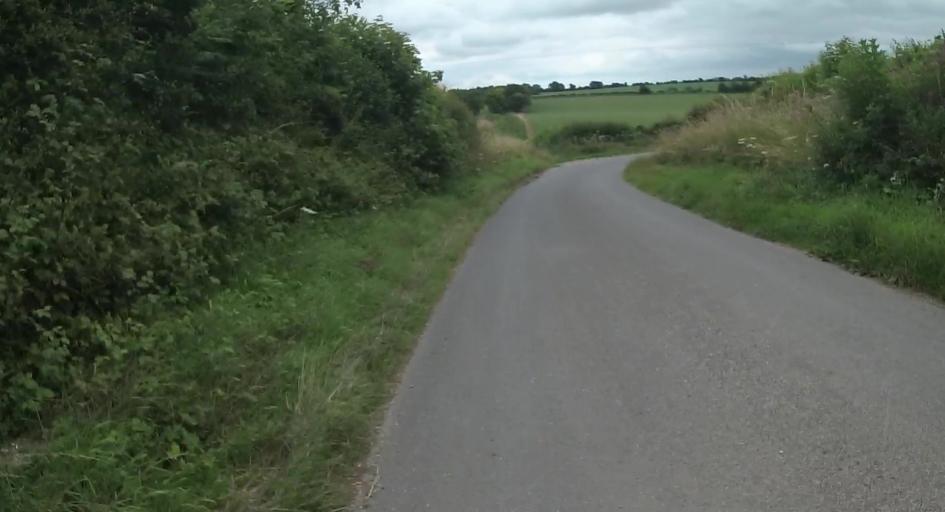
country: GB
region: England
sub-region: Hampshire
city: Four Marks
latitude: 51.0655
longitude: -1.1510
